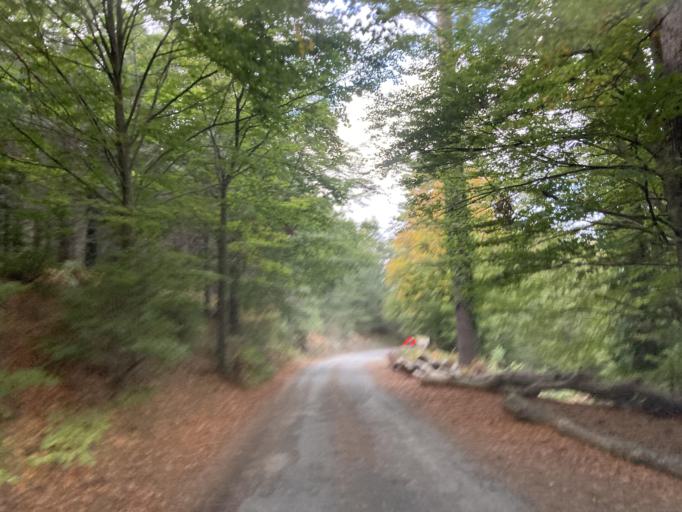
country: FR
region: Languedoc-Roussillon
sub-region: Departement des Pyrenees-Orientales
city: la Roca d'Albera
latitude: 42.4786
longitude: 2.9293
